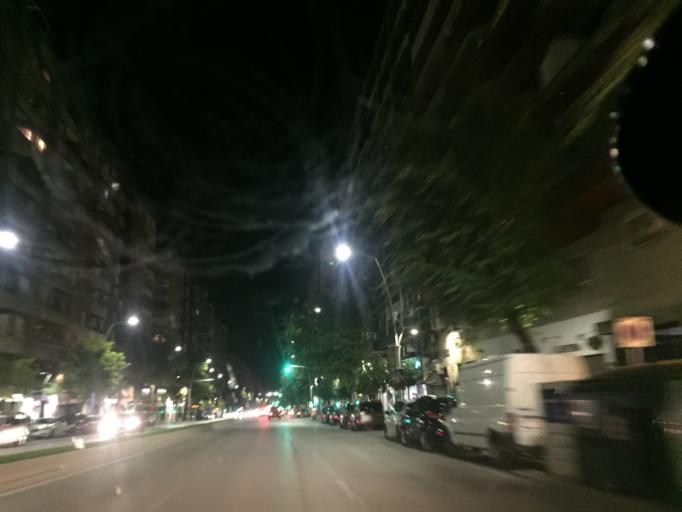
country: ES
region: Andalusia
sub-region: Provincia de Jaen
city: Jaen
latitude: 37.7779
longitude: -3.8002
